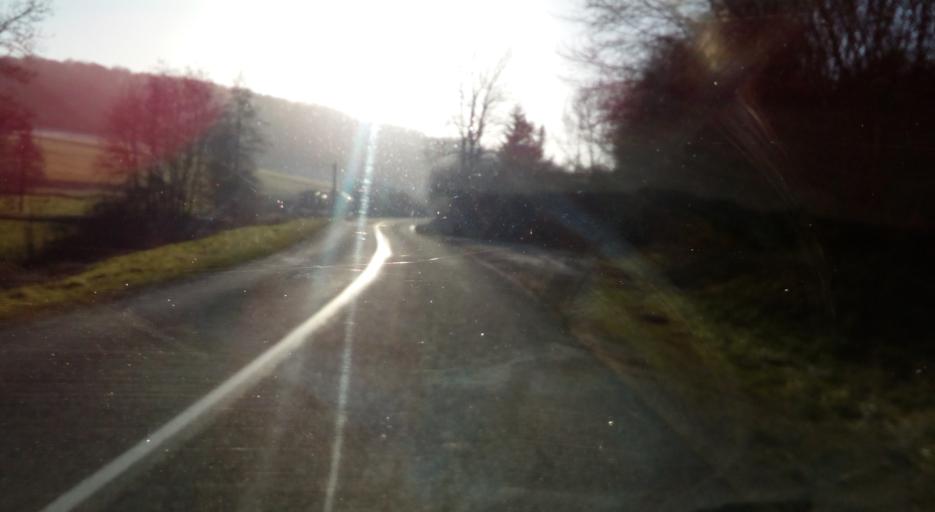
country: FR
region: Champagne-Ardenne
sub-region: Departement des Ardennes
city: Rimogne
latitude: 49.7787
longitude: 4.4598
